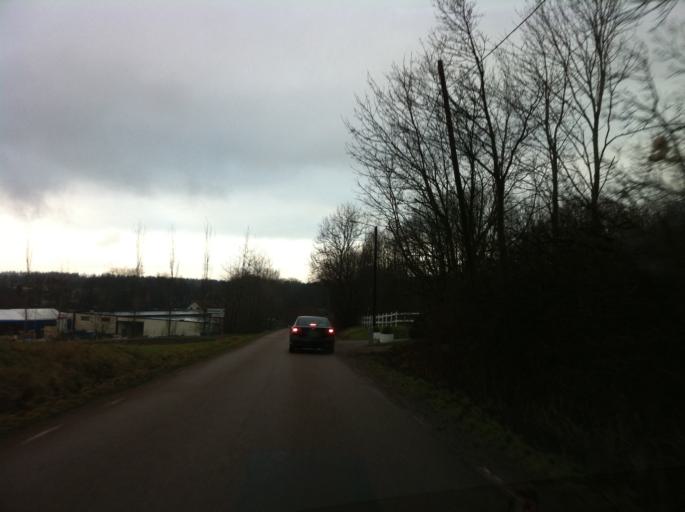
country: SE
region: Skane
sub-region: Helsingborg
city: Barslov
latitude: 55.9897
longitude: 12.8259
